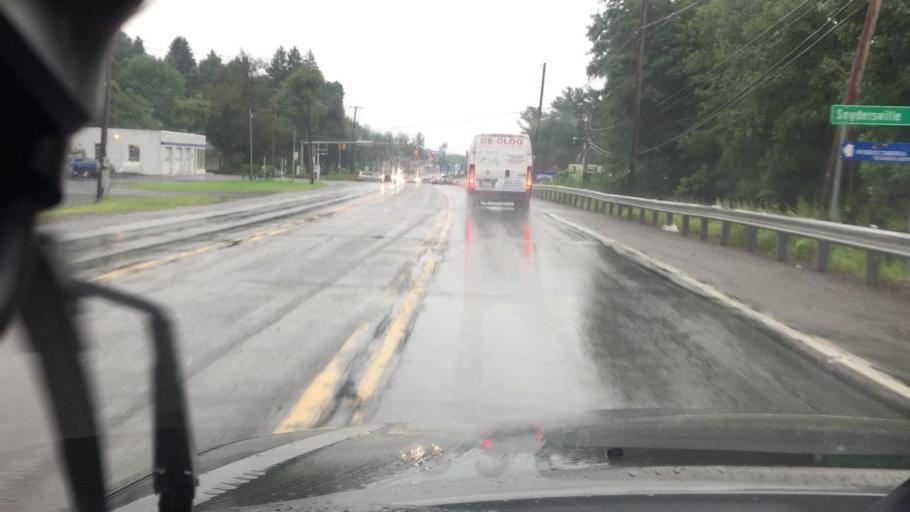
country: US
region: Pennsylvania
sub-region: Monroe County
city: Tannersville
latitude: 41.0055
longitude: -75.2814
